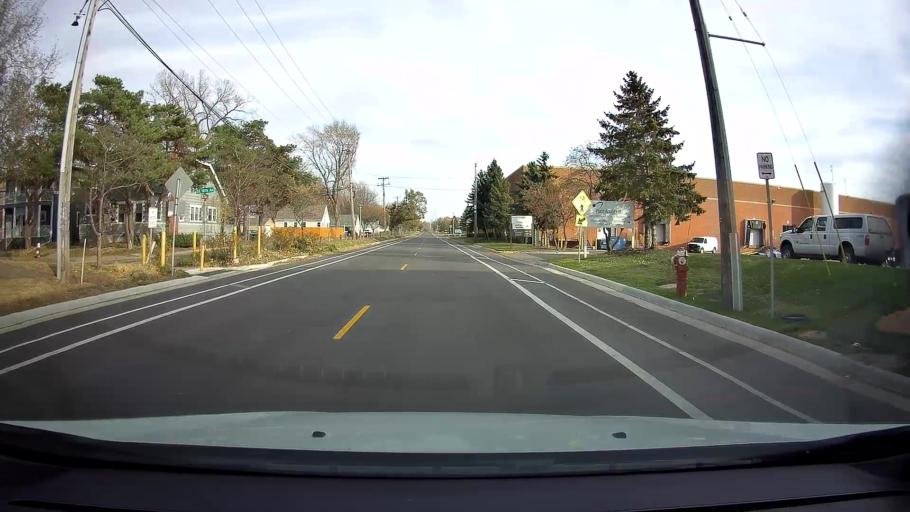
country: US
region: Minnesota
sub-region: Ramsey County
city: Lauderdale
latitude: 44.9842
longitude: -93.2268
